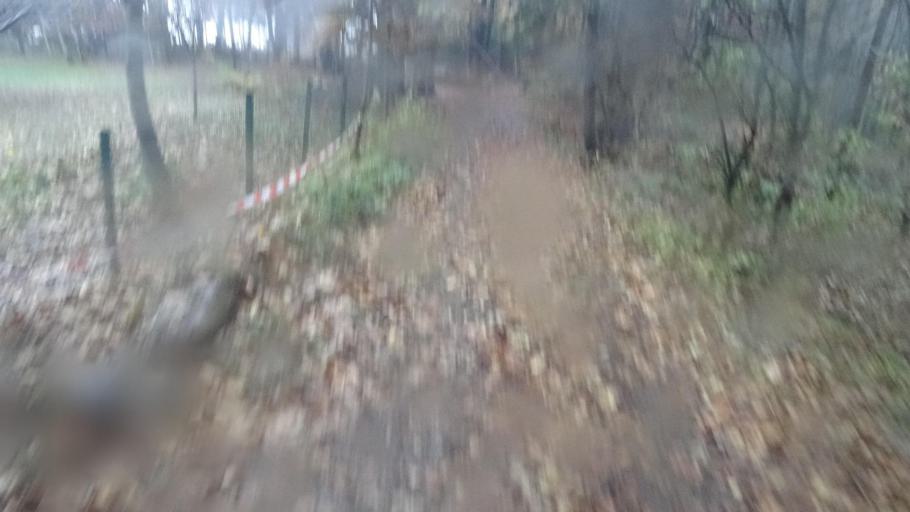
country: DE
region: Rheinland-Pfalz
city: Birkheim
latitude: 50.1018
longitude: 7.5995
